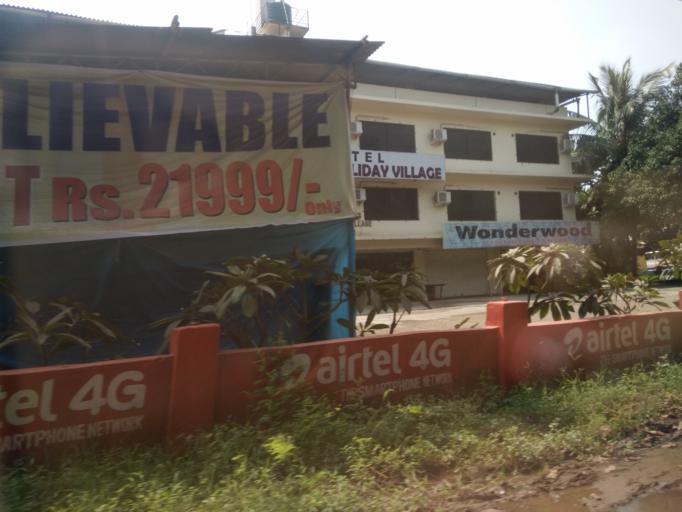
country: IN
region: Goa
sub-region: South Goa
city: Cortalim
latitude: 15.4196
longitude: 73.9028
